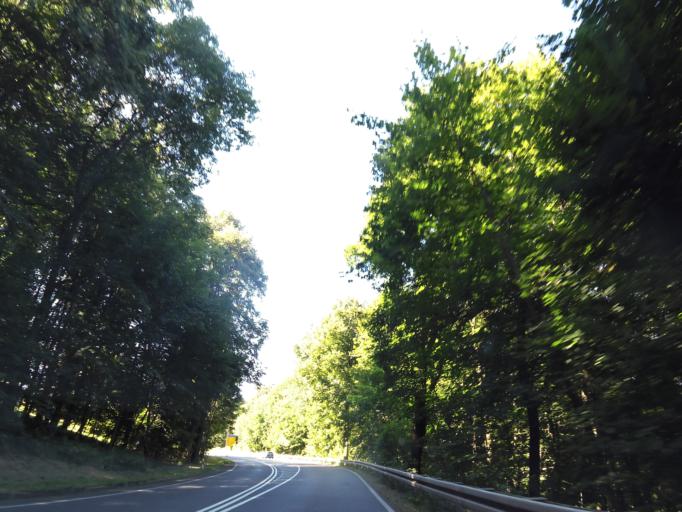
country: DE
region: Saxony
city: Konigstein
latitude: 50.9252
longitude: 14.0542
